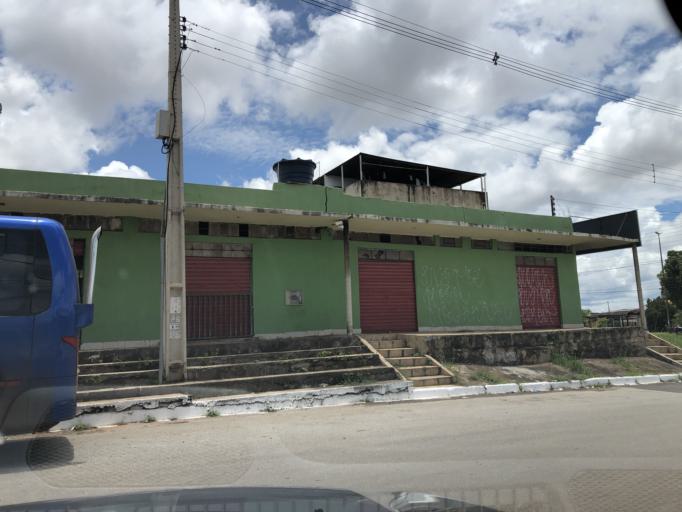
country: BR
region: Federal District
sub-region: Brasilia
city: Brasilia
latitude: -15.8354
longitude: -48.0953
